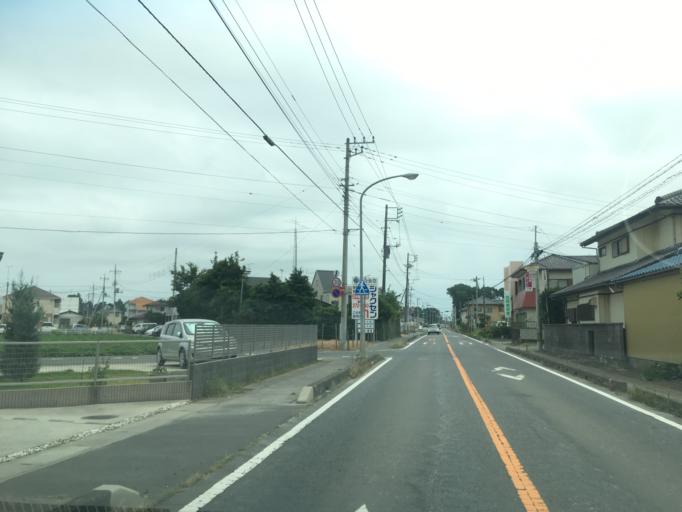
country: JP
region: Ibaraki
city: Katsuta
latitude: 36.3832
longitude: 140.5448
